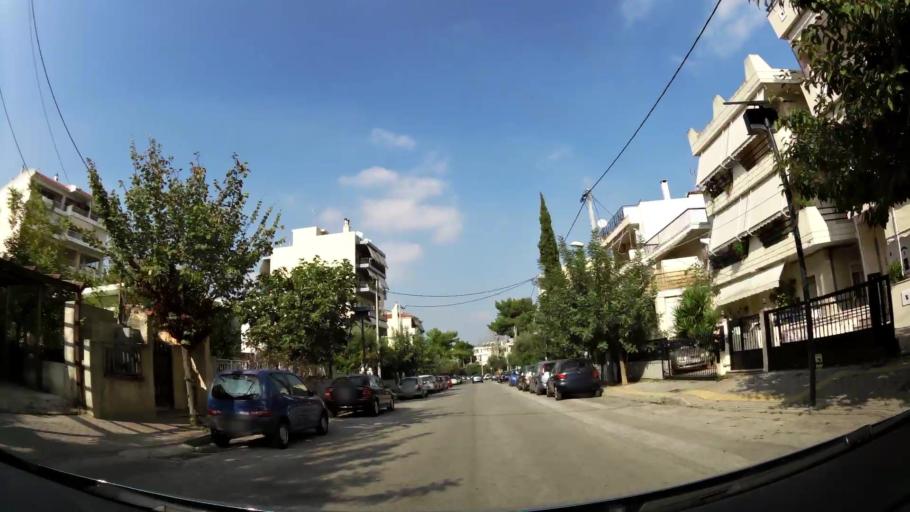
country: GR
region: Attica
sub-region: Nomarchia Athinas
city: Cholargos
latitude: 37.9987
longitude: 23.8106
